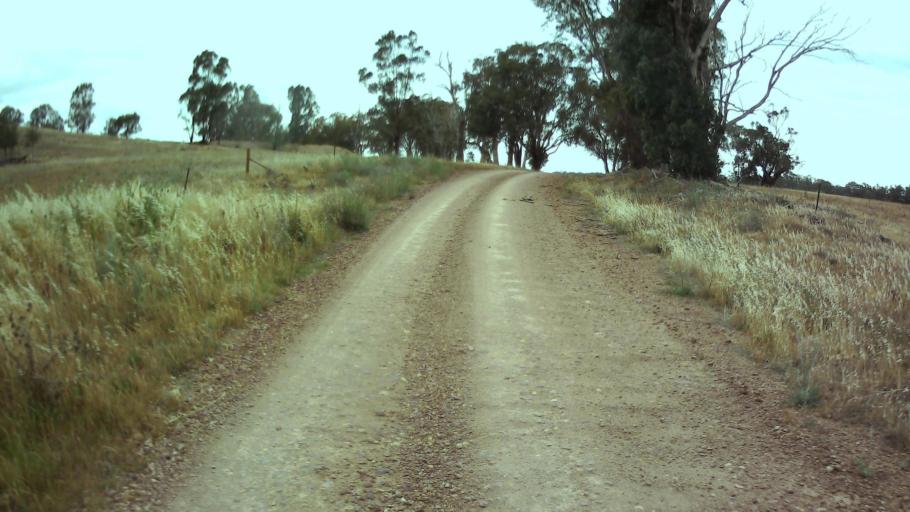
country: AU
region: New South Wales
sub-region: Weddin
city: Grenfell
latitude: -33.9127
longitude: 148.2893
